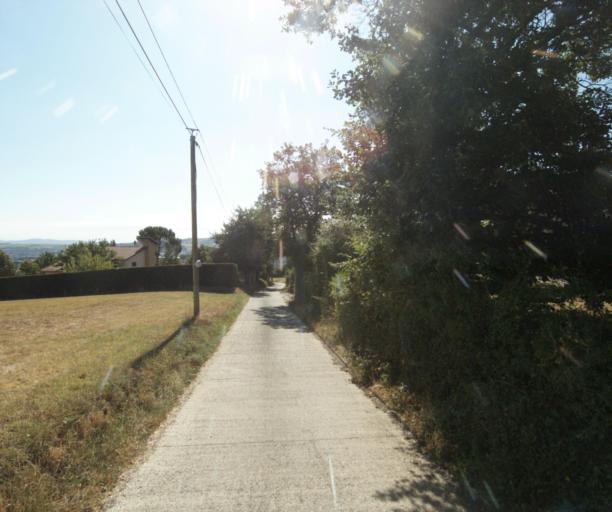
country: FR
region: Rhone-Alpes
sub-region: Departement du Rhone
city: Savigny
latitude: 45.8207
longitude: 4.5684
